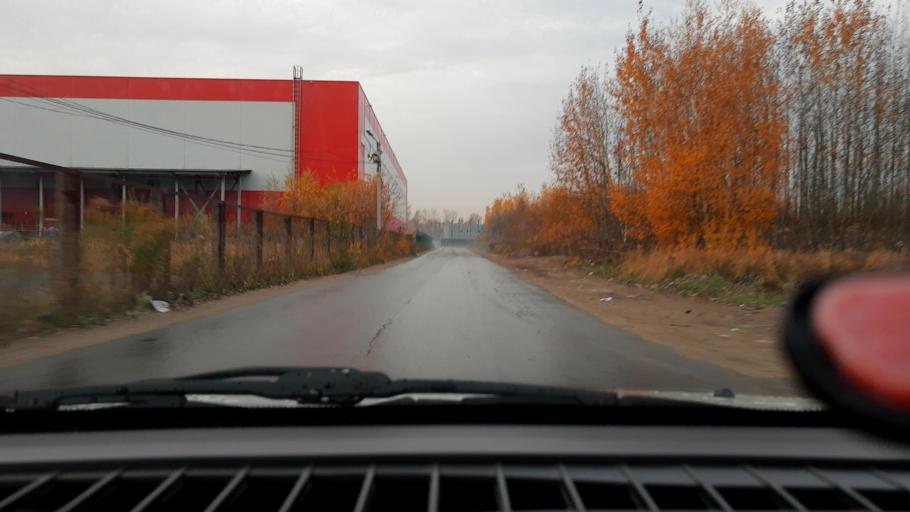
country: RU
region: Nizjnij Novgorod
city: Gorbatovka
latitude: 56.3178
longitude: 43.8515
